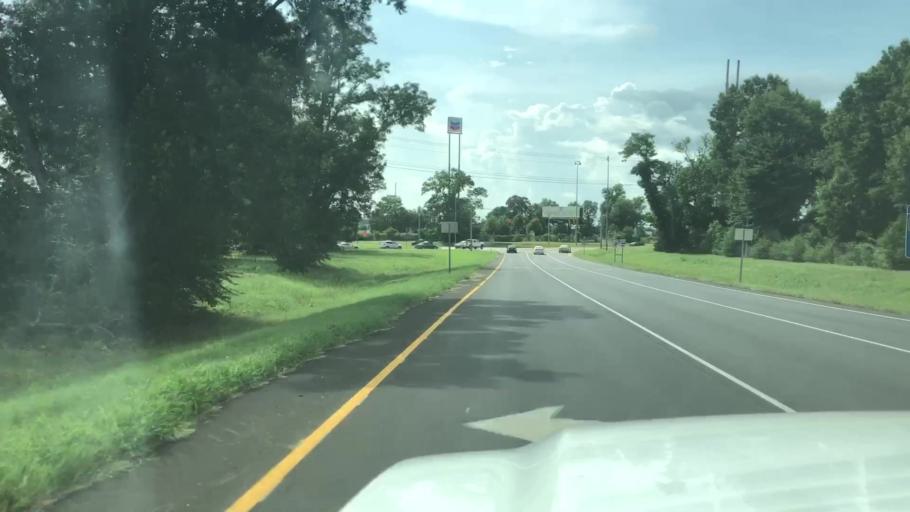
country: US
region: Alabama
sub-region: Montgomery County
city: Pike Road
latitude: 32.3685
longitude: -86.1373
